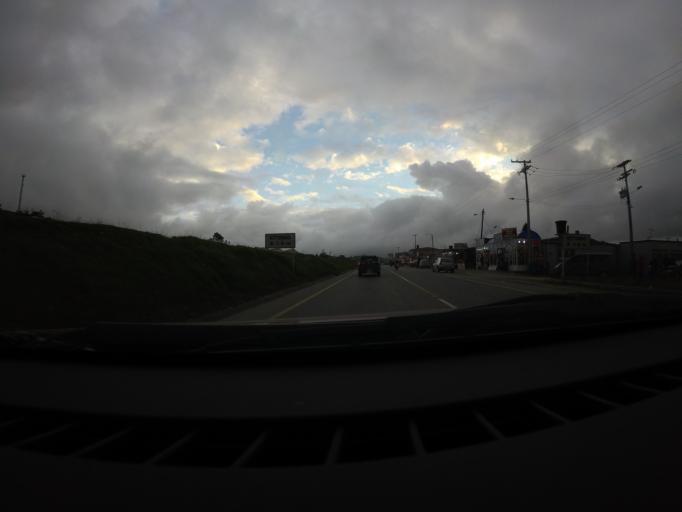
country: CO
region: Boyaca
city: Samaca
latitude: 5.4270
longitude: -73.4508
